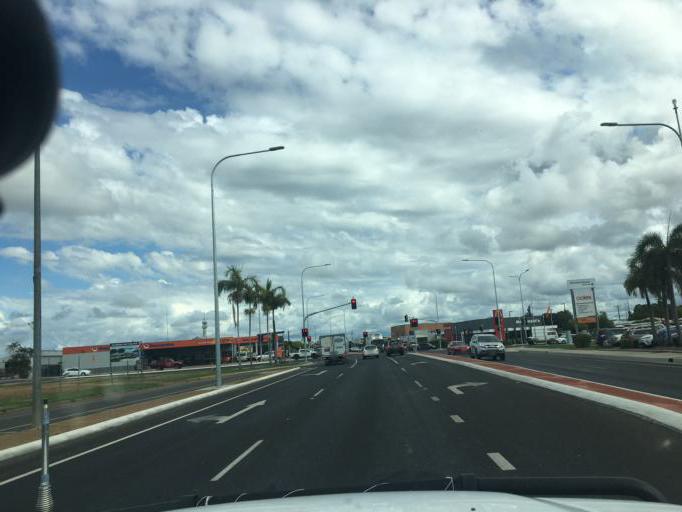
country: AU
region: Queensland
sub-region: Tablelands
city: Mareeba
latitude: -16.9983
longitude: 145.4230
